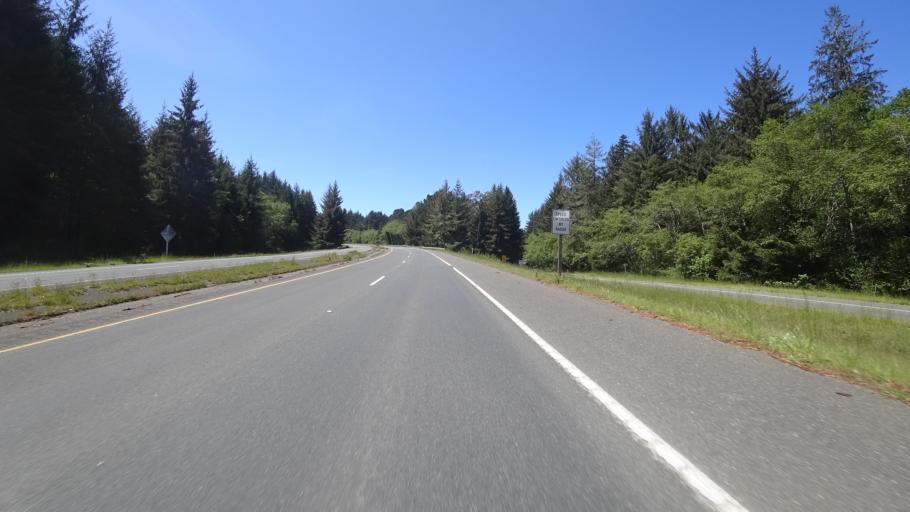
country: US
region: California
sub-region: Humboldt County
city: Westhaven-Moonstone
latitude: 41.1369
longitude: -124.1452
